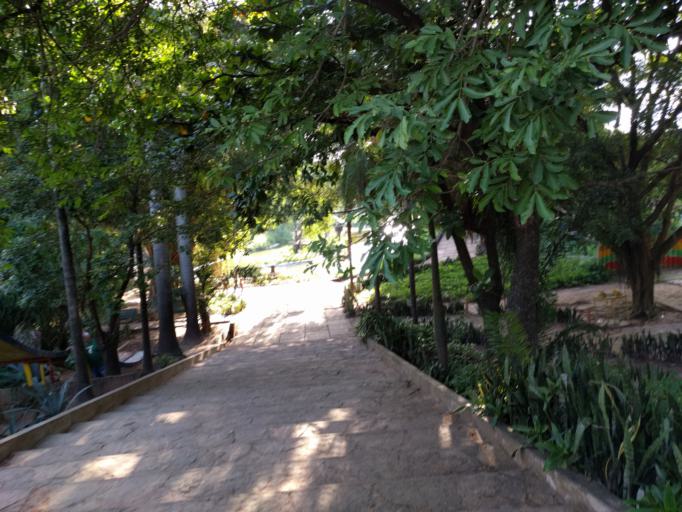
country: BO
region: Santa Cruz
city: Santa Cruz de la Sierra
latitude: -17.7600
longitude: -63.1858
